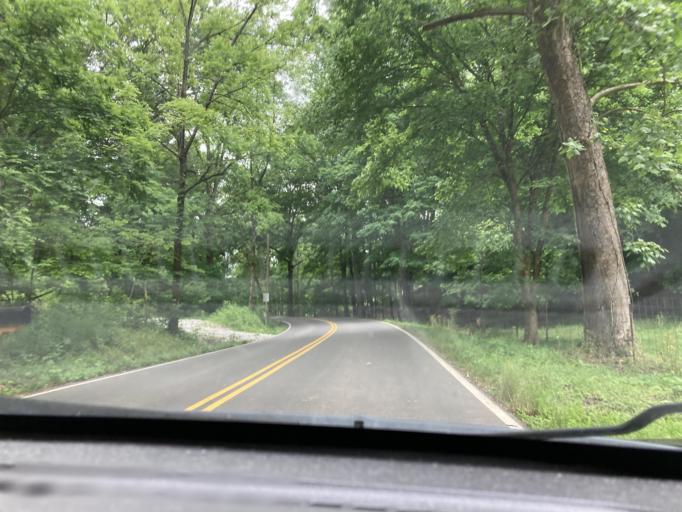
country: US
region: Tennessee
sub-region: Dickson County
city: Dickson
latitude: 36.0381
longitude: -87.3668
